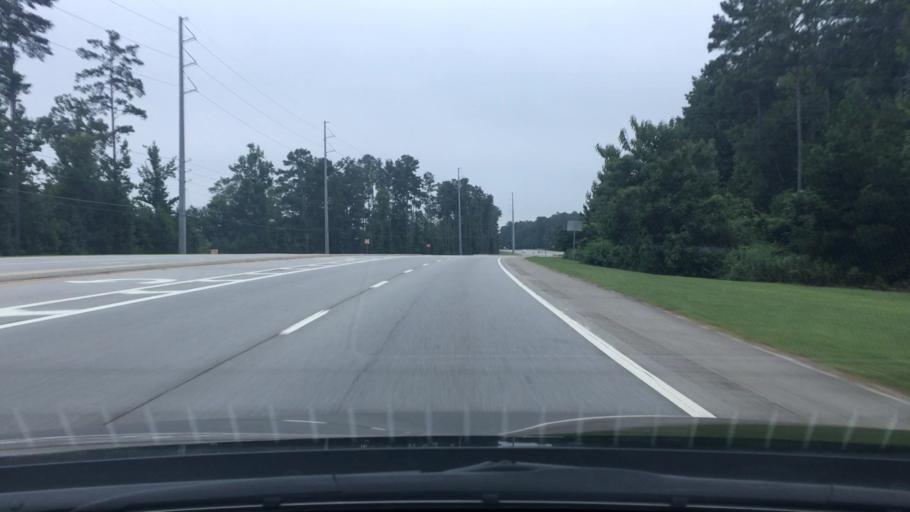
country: US
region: Georgia
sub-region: Coweta County
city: Senoia
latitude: 33.3485
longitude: -84.5493
